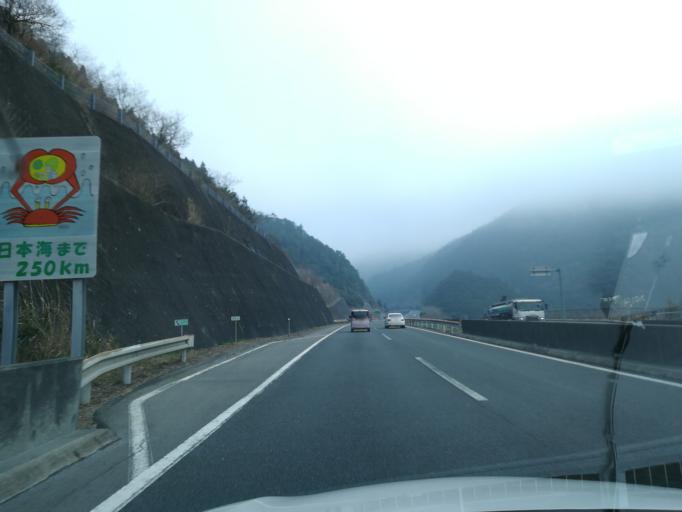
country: JP
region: Ehime
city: Kawanoecho
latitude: 33.7844
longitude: 133.6624
